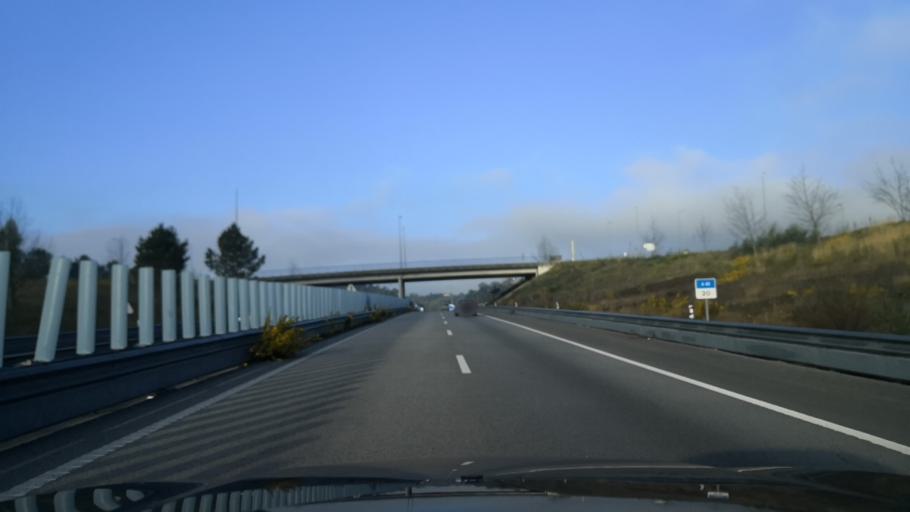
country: PT
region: Porto
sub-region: Lousada
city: Lousada
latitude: 41.2920
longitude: -8.2743
